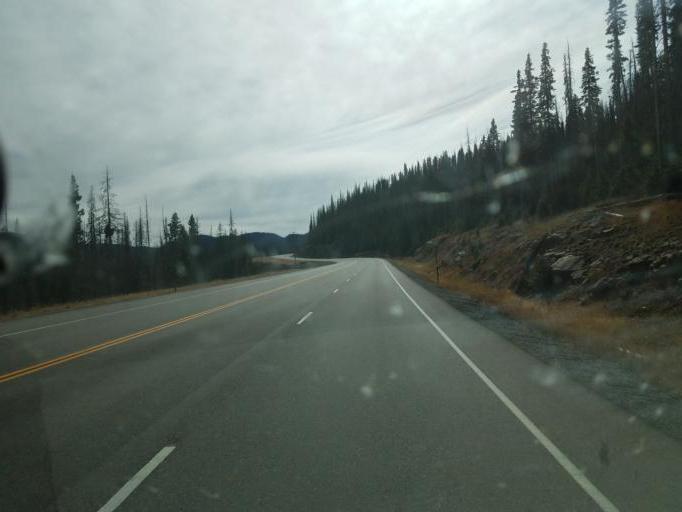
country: US
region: Colorado
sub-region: Archuleta County
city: Pagosa Springs
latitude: 37.5013
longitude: -106.7710
